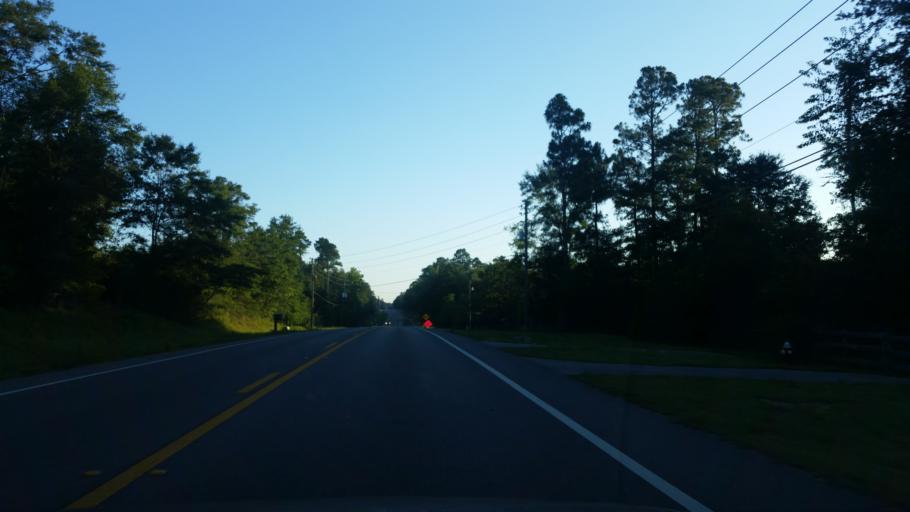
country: US
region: Florida
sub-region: Escambia County
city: Cantonment
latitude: 30.5810
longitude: -87.3283
